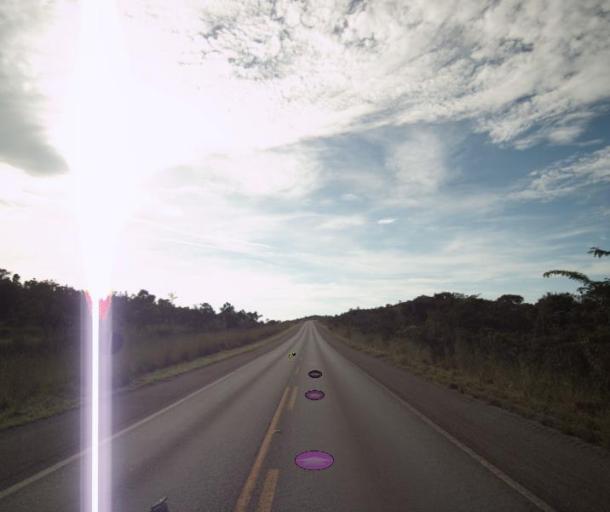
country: BR
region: Goias
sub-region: Pirenopolis
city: Pirenopolis
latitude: -15.7526
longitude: -48.5895
